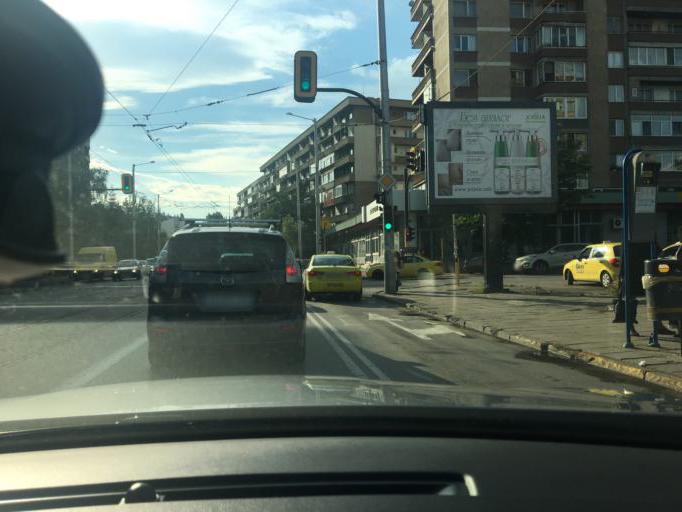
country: BG
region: Sofia-Capital
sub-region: Stolichna Obshtina
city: Sofia
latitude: 42.6784
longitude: 23.3659
